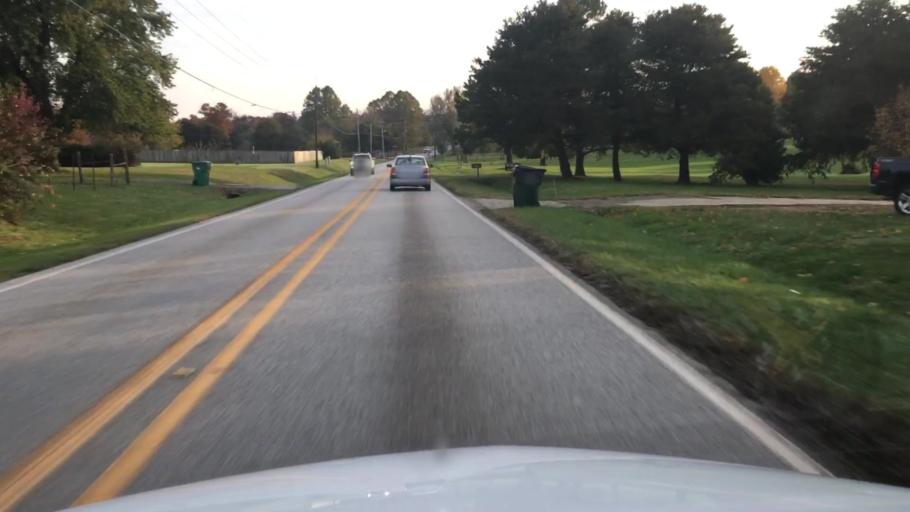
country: US
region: Arkansas
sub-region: Washington County
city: Elm Springs
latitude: 36.2190
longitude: -94.2306
